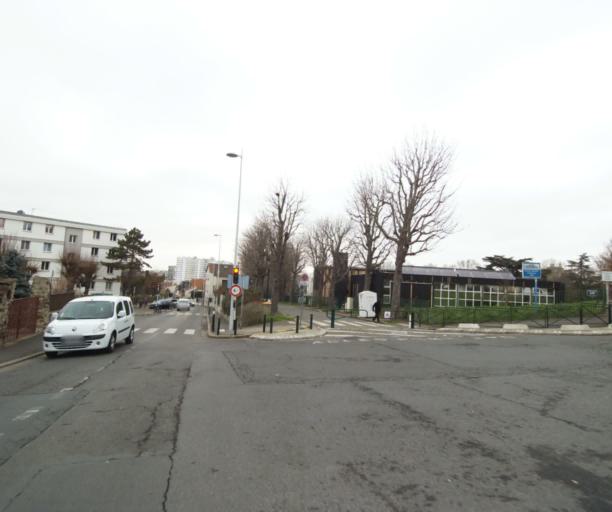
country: FR
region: Ile-de-France
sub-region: Departement des Hauts-de-Seine
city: Nanterre
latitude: 48.8831
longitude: 2.2013
